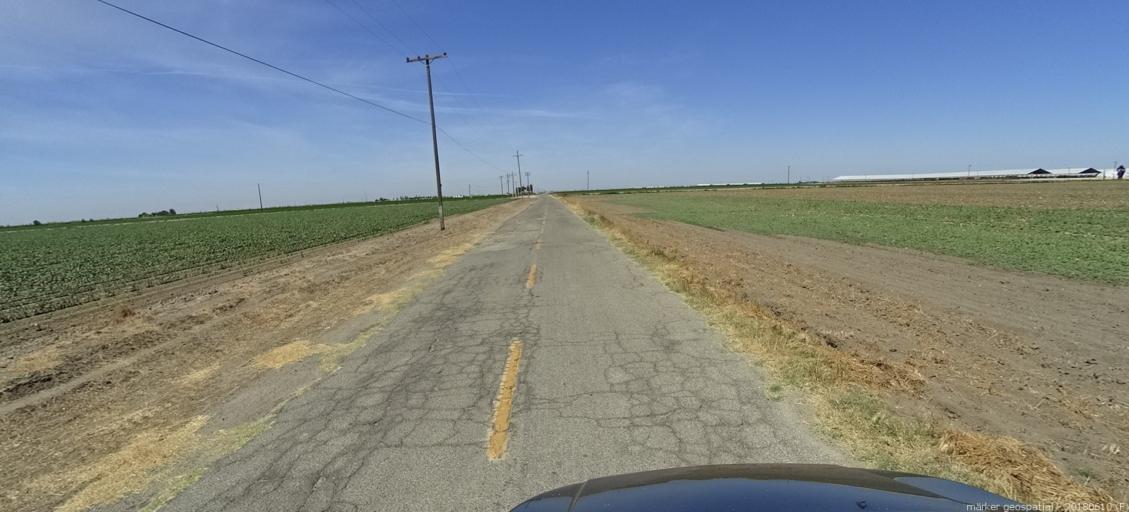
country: US
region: California
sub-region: Merced County
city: Dos Palos
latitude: 37.0546
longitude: -120.4435
